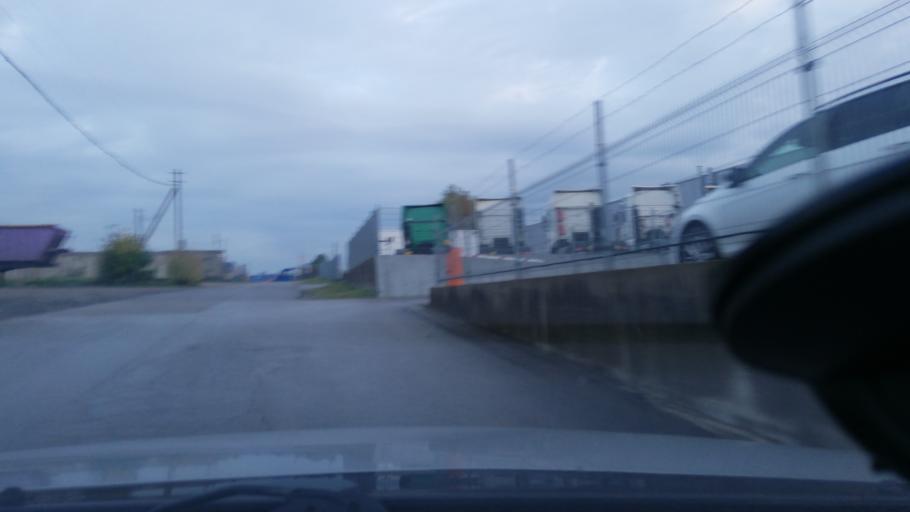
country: LT
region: Klaipedos apskritis
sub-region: Klaipeda
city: Klaipeda
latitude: 55.6867
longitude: 21.1856
